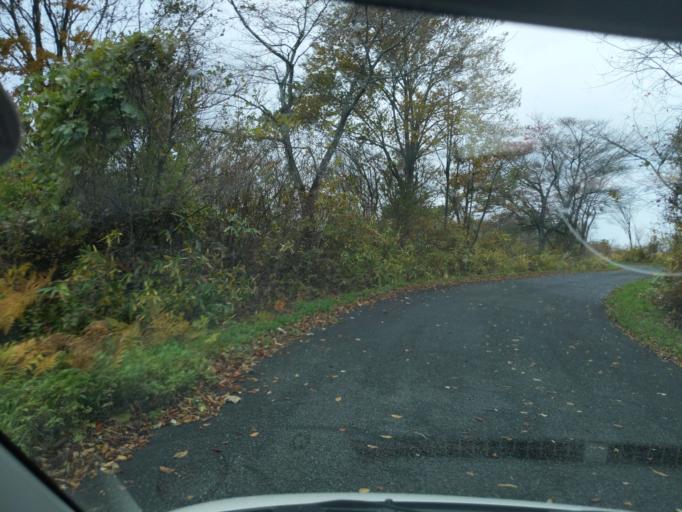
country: JP
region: Iwate
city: Mizusawa
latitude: 39.0705
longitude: 141.0383
